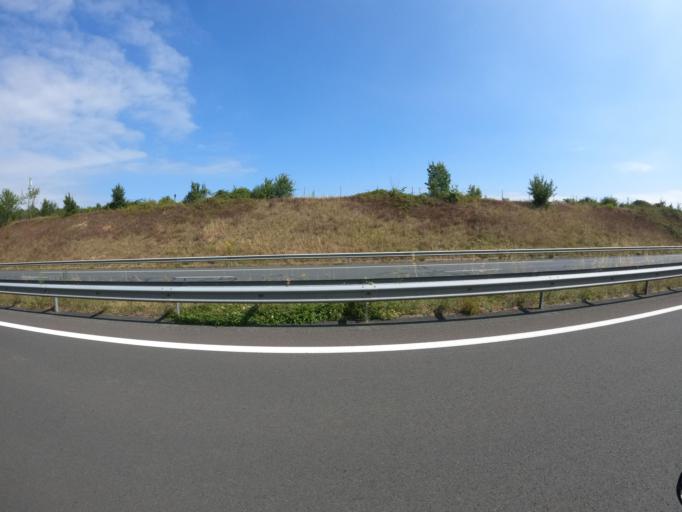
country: FR
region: Poitou-Charentes
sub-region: Departement de la Charente-Maritime
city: Courcon
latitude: 46.2146
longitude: -0.7684
